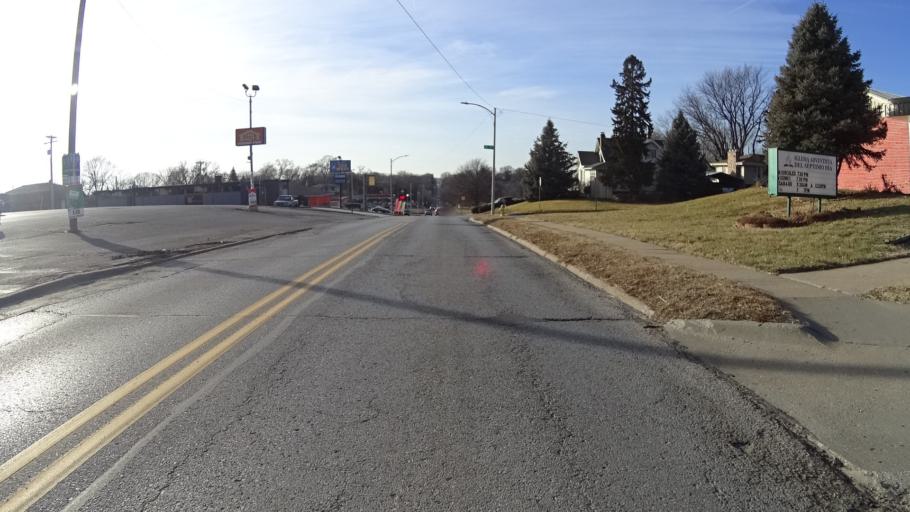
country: US
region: Nebraska
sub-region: Sarpy County
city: La Vista
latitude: 41.1909
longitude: -95.9741
